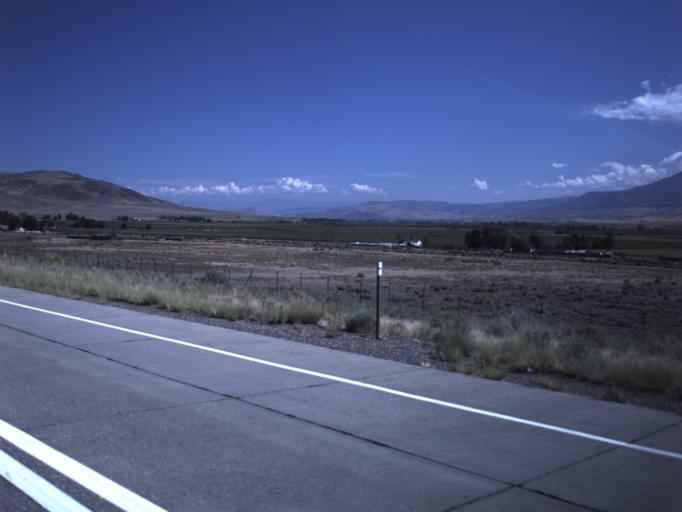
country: US
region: Utah
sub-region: Sevier County
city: Monroe
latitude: 38.6328
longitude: -112.2228
